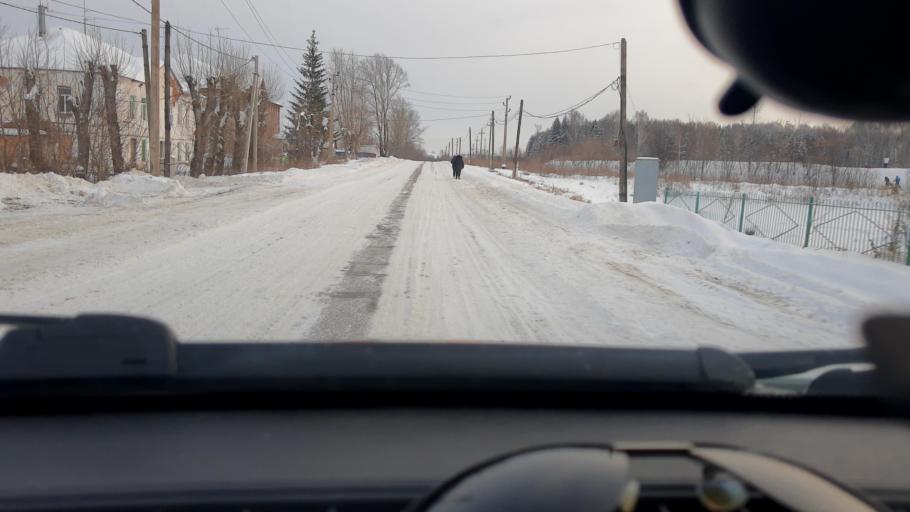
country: RU
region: Bashkortostan
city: Yazykovo
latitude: 55.0446
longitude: 56.1837
